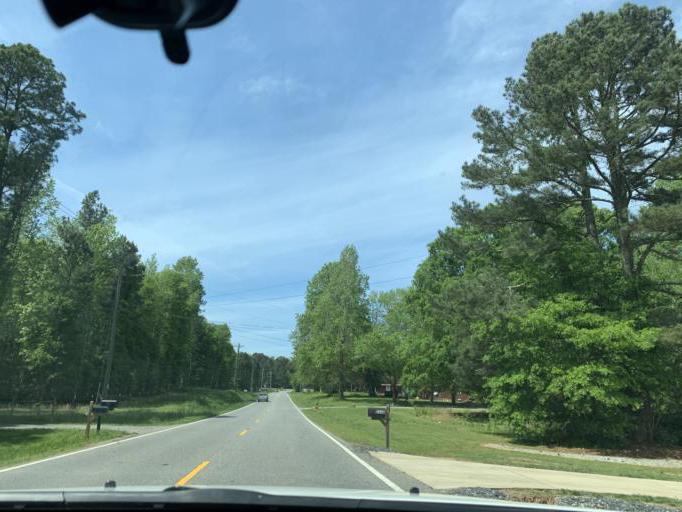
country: US
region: Georgia
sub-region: Forsyth County
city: Cumming
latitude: 34.2643
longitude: -84.1735
